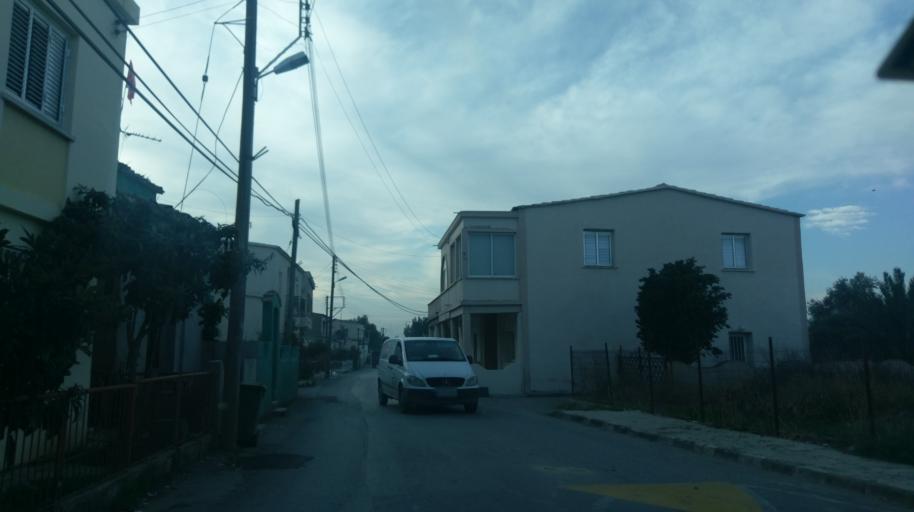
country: CY
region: Larnaka
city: Athienou
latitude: 35.1595
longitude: 33.6050
